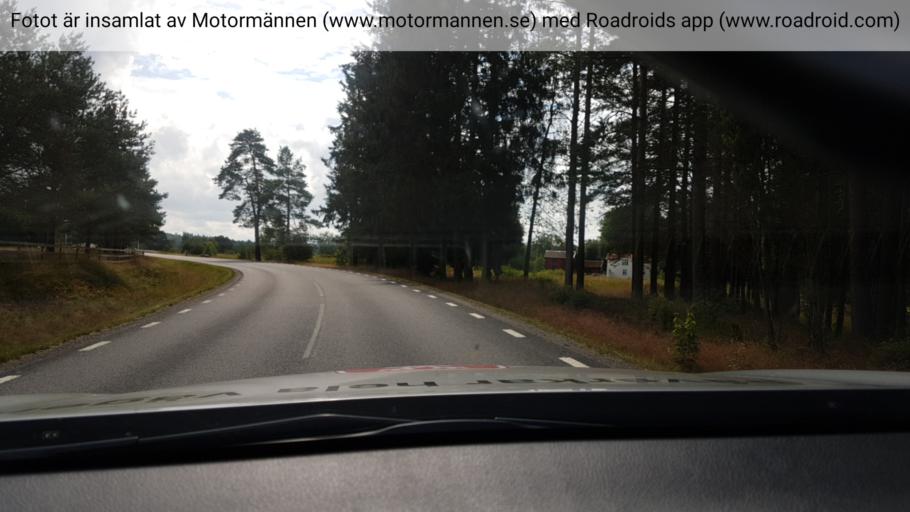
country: SE
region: Vaestra Goetaland
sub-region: Svenljunga Kommun
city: Svenljunga
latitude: 57.4658
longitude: 13.1719
